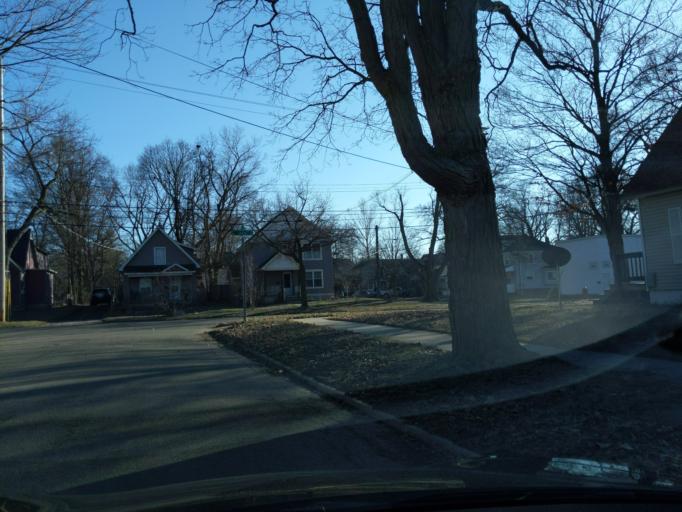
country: US
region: Michigan
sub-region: Ingham County
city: Lansing
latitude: 42.7364
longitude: -84.5699
